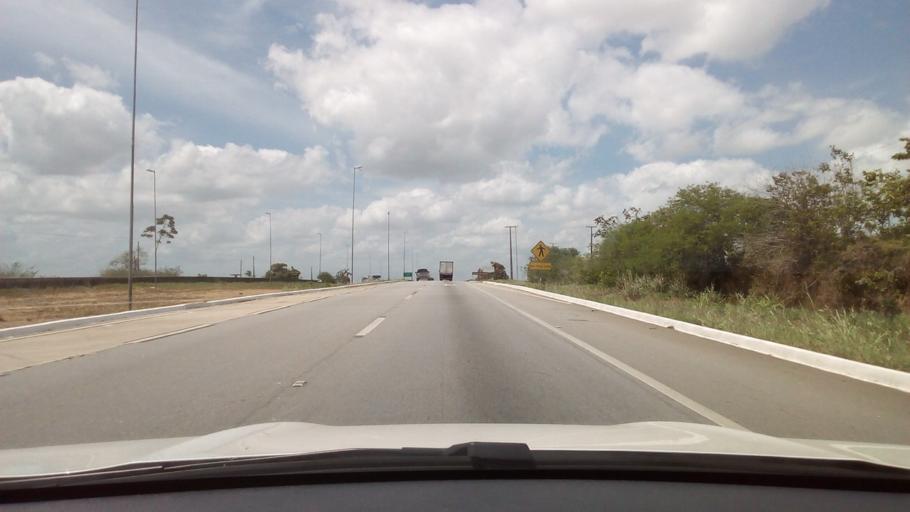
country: BR
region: Paraiba
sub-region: Mamanguape
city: Mamanguape
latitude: -6.9327
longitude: -35.1023
